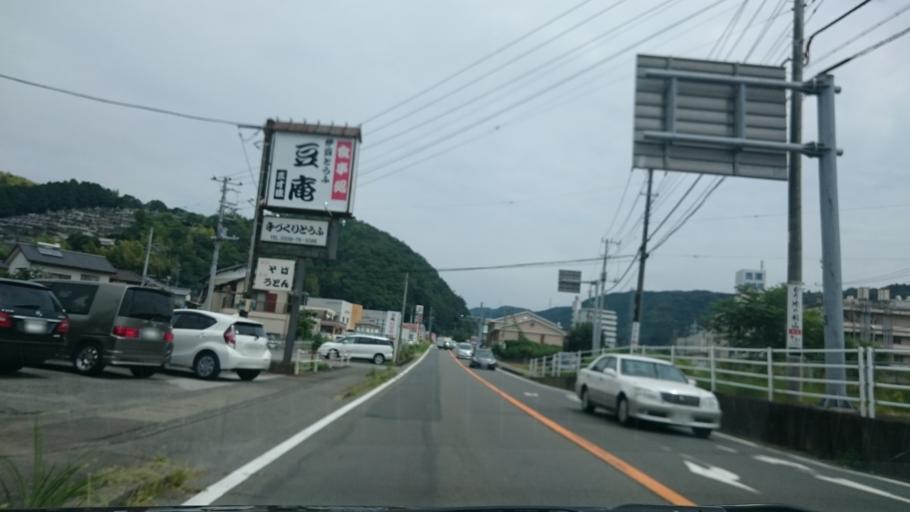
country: JP
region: Shizuoka
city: Mishima
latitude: 35.0091
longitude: 138.9471
